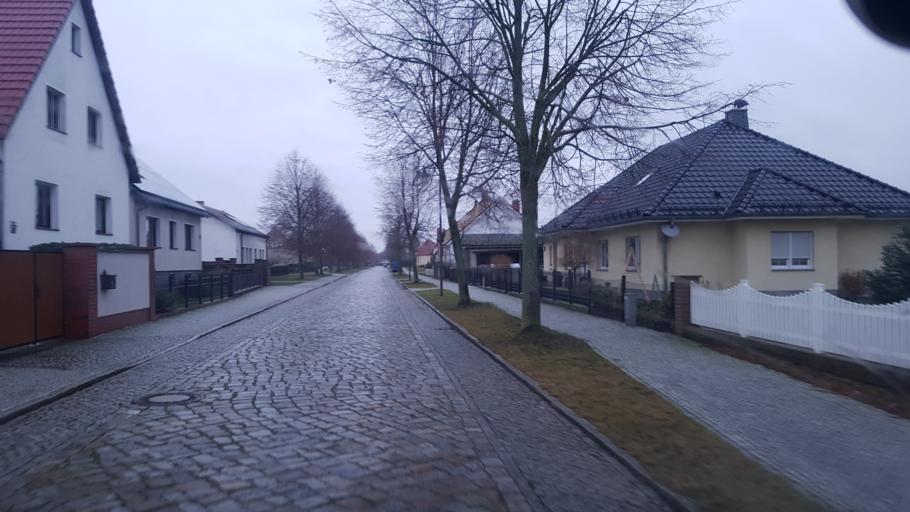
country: DE
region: Brandenburg
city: Ludwigsfelde
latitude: 52.3161
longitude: 13.1940
